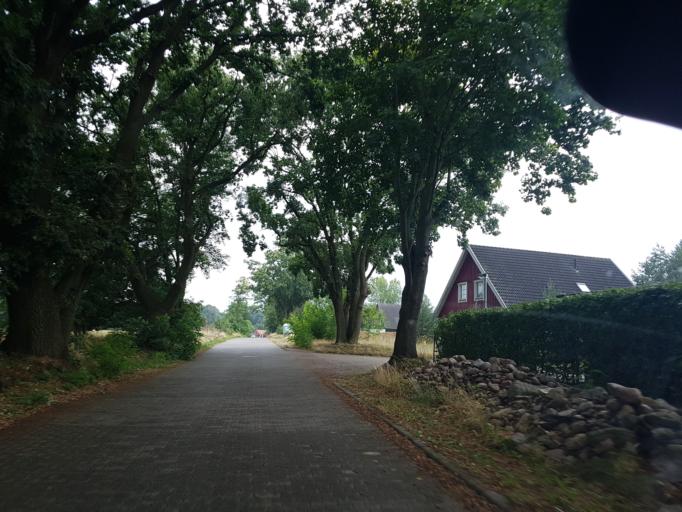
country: DE
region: Saxony-Anhalt
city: Loburg
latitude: 52.2452
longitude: 12.0460
